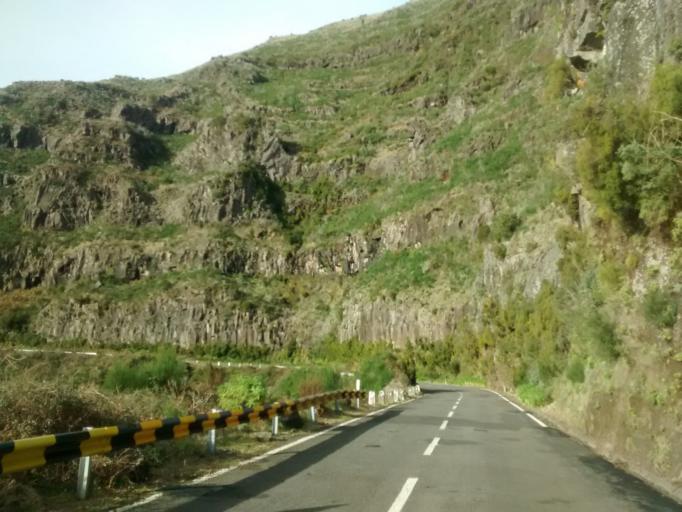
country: PT
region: Madeira
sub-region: Sao Vicente
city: Sao Vicente
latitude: 32.7401
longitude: -17.0488
